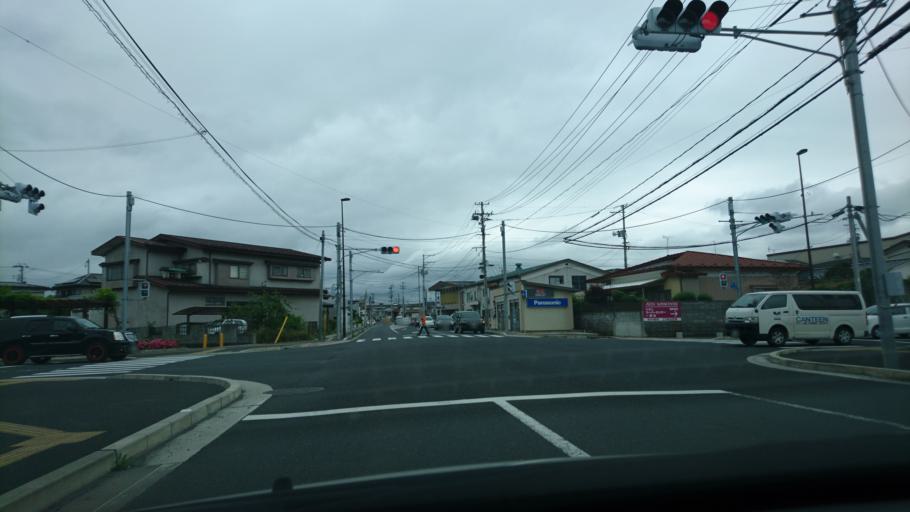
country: JP
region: Iwate
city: Ichinoseki
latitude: 38.9297
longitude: 141.1475
